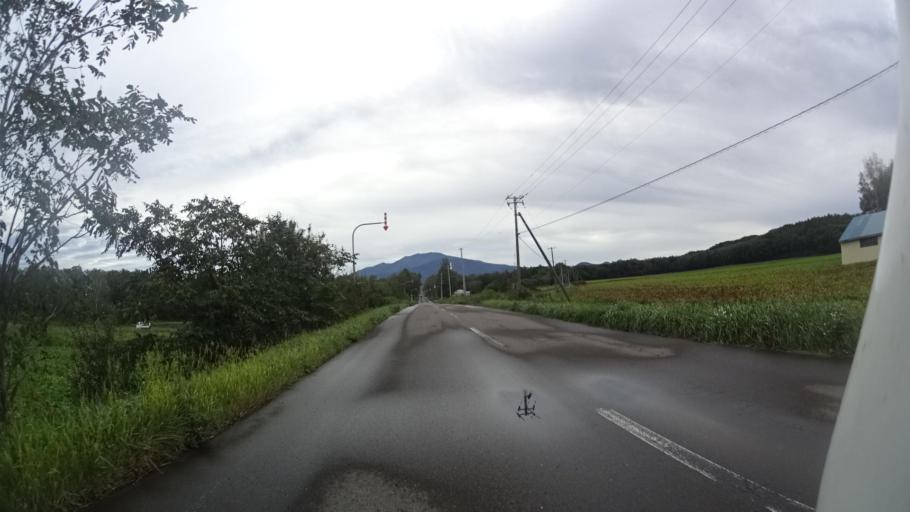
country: JP
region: Hokkaido
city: Shibetsu
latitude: 43.8730
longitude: 144.7153
